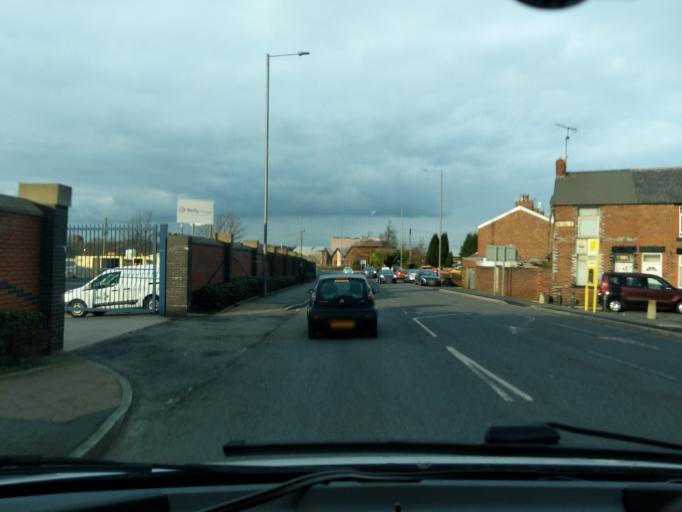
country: GB
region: England
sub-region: St. Helens
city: St Helens
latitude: 53.4535
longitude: -2.7247
